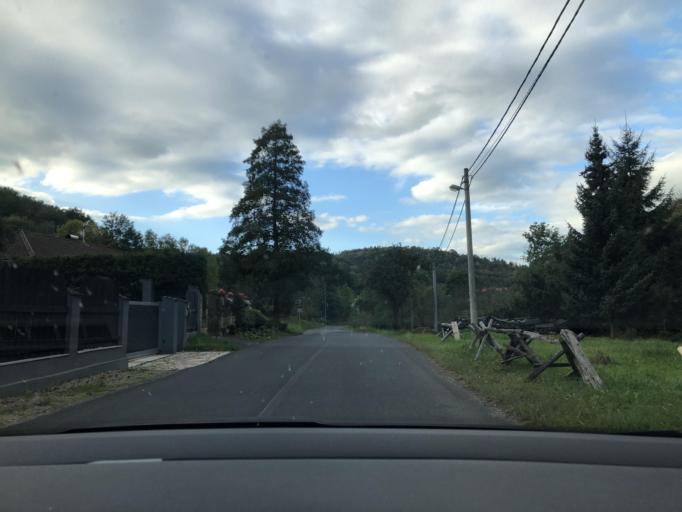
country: CZ
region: Ustecky
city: Velke Brezno
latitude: 50.6517
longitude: 14.1413
